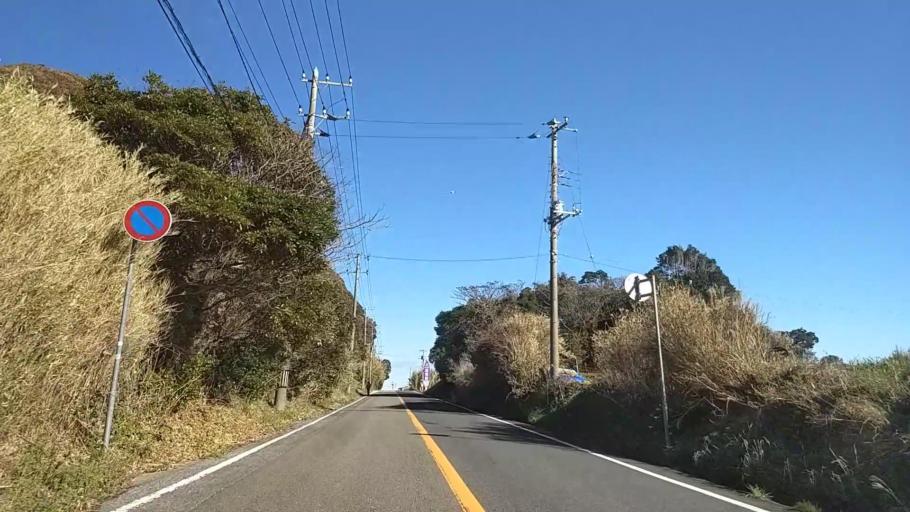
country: JP
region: Chiba
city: Tateyama
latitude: 34.9164
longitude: 139.9335
